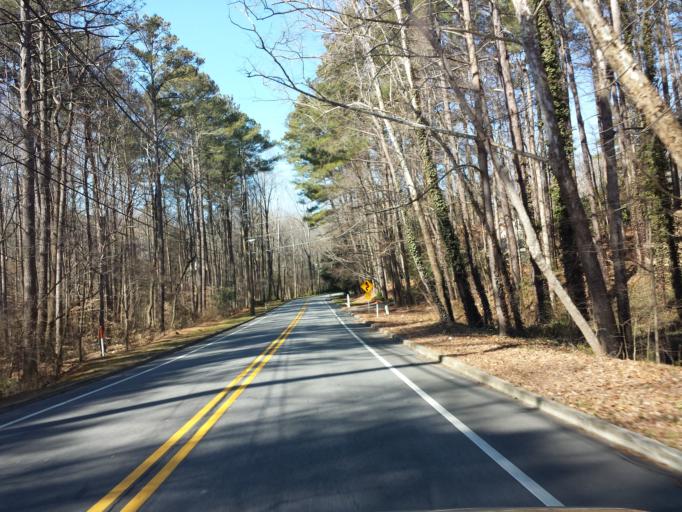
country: US
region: Georgia
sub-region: Fulton County
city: Sandy Springs
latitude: 33.9141
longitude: -84.4334
